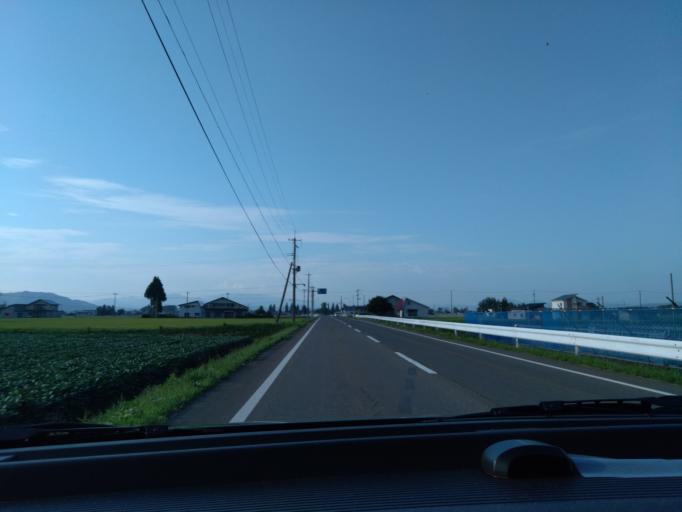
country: JP
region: Akita
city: Kakunodatemachi
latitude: 39.5032
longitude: 140.5598
